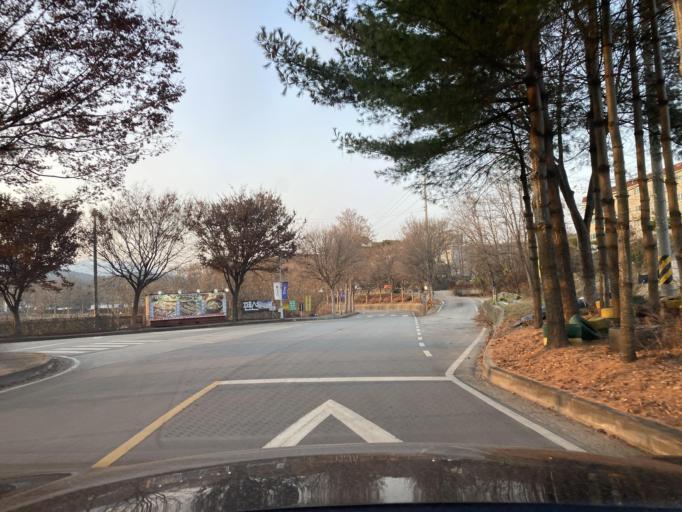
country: KR
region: Chungcheongnam-do
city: Hongsung
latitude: 36.6937
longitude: 126.6599
